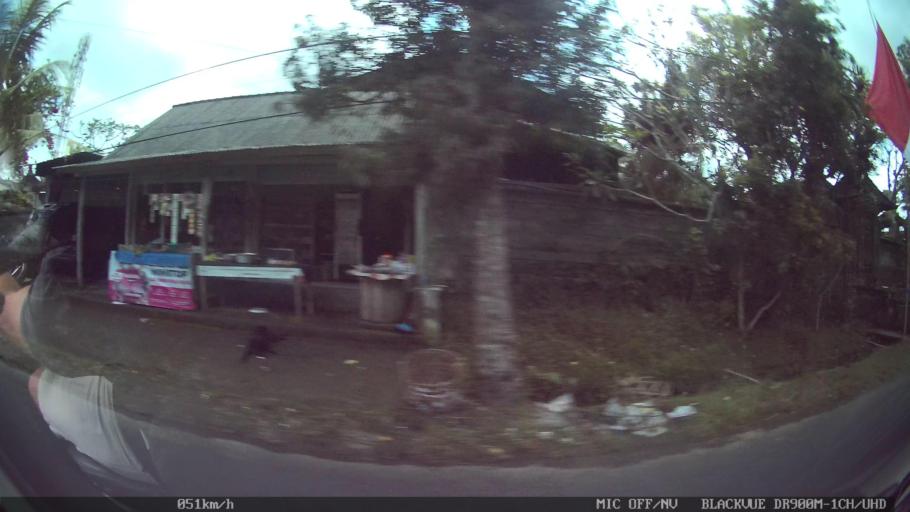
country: ID
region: Bali
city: Banjar Madangan Kaja
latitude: -8.4763
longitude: 115.3238
